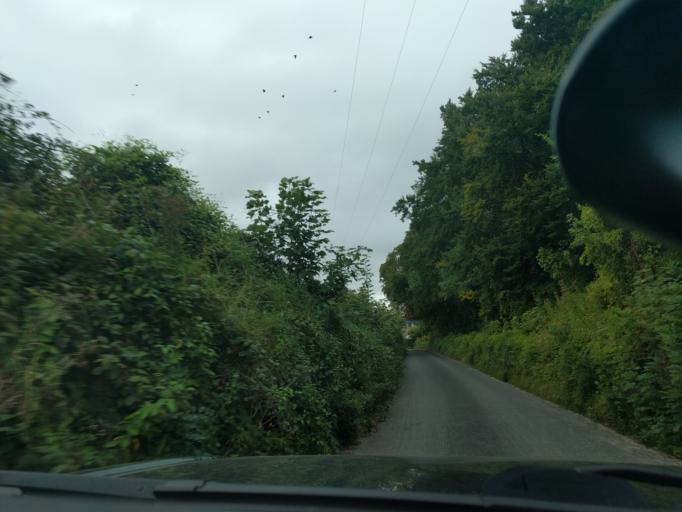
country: GB
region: England
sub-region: Wiltshire
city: Corsham
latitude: 51.4139
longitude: -2.1789
